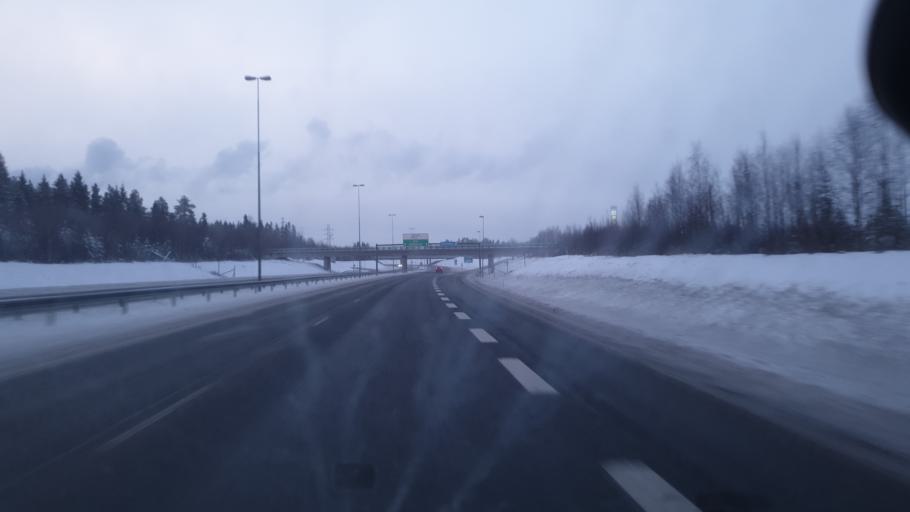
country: FI
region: Lapland
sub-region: Kemi-Tornio
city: Keminmaa
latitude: 65.8025
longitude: 24.5139
